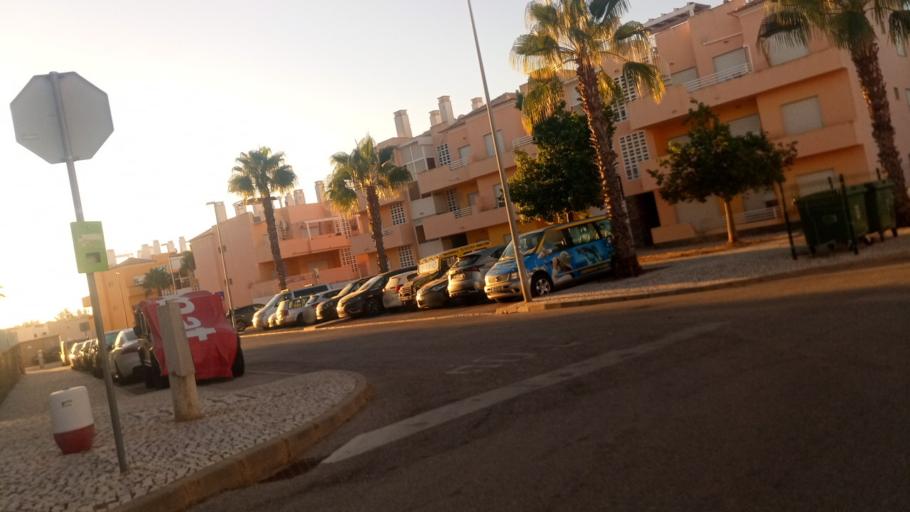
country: PT
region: Faro
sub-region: Tavira
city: Tavira
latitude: 37.1454
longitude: -7.6087
